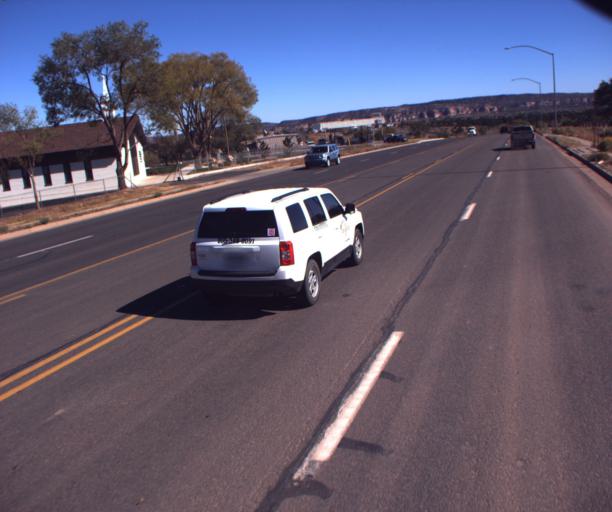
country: US
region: Arizona
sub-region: Apache County
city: Saint Michaels
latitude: 35.6569
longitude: -109.1099
